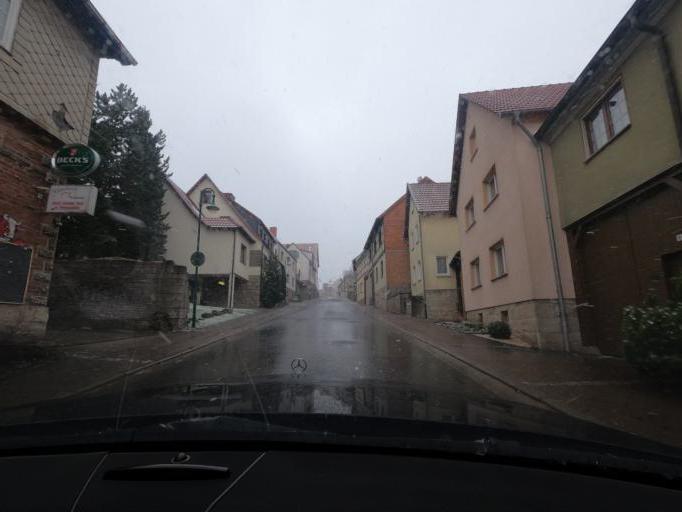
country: DE
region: Thuringia
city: Effelder
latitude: 51.2400
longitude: 10.2470
